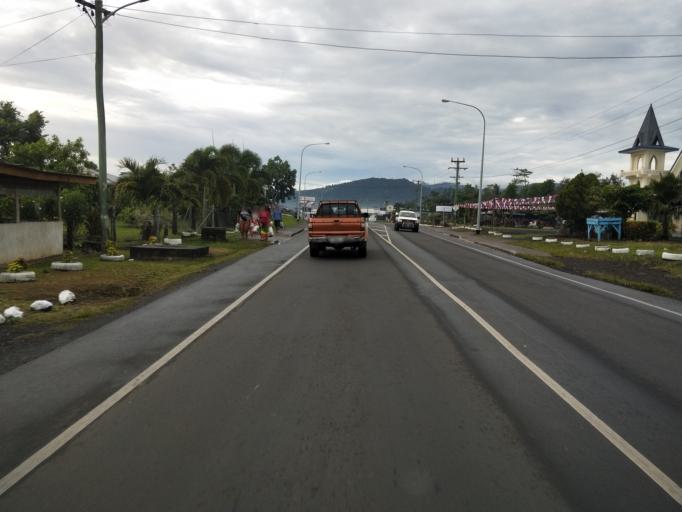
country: WS
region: Tuamasaga
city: Vaiusu
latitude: -13.8172
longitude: -171.8077
